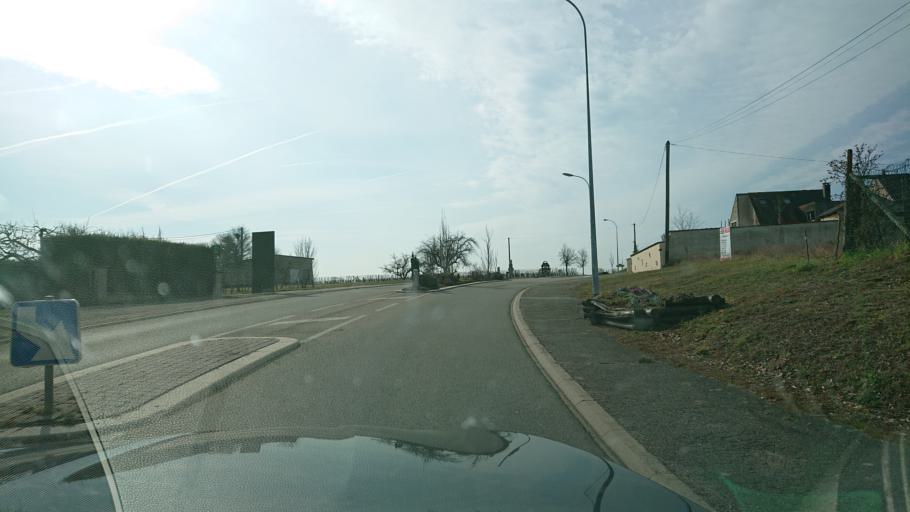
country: FR
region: Alsace
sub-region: Departement du Bas-Rhin
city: Chatenois
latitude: 48.2645
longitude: 7.3997
